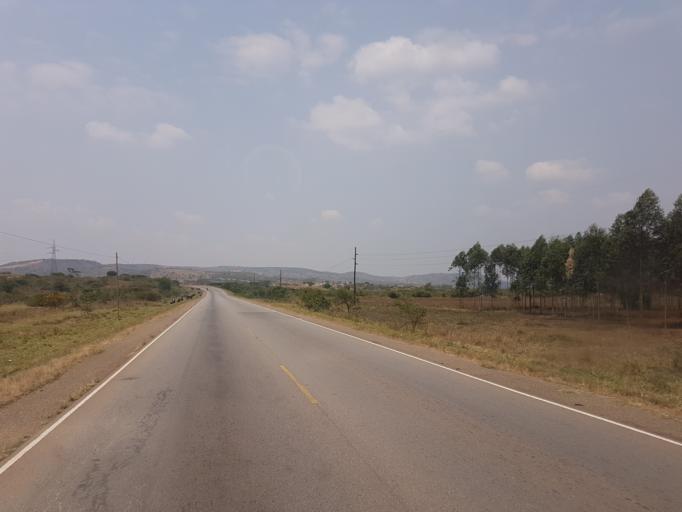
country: UG
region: Western Region
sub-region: Mbarara District
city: Mbarara
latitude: -0.5097
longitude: 30.8352
